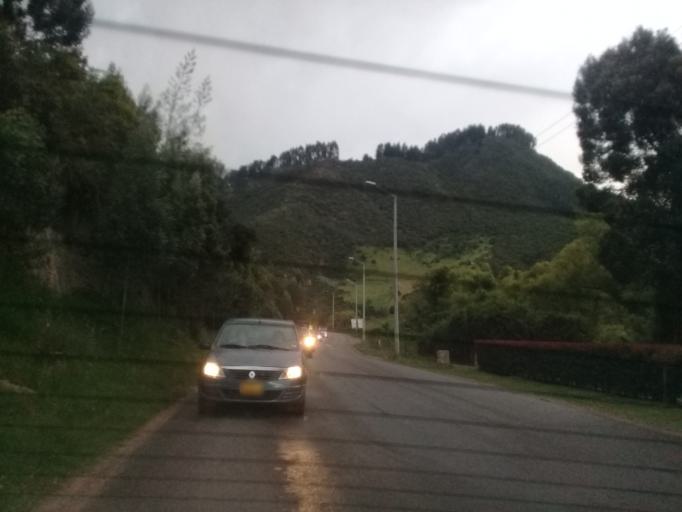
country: CO
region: Cundinamarca
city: Tabio
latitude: 4.9257
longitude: -74.0676
